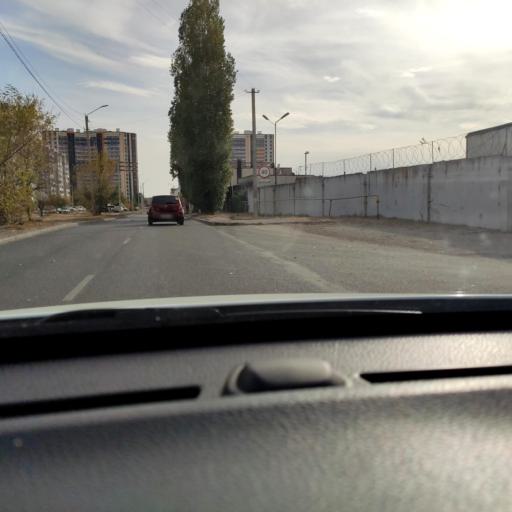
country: RU
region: Voronezj
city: Maslovka
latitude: 51.5925
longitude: 39.2436
